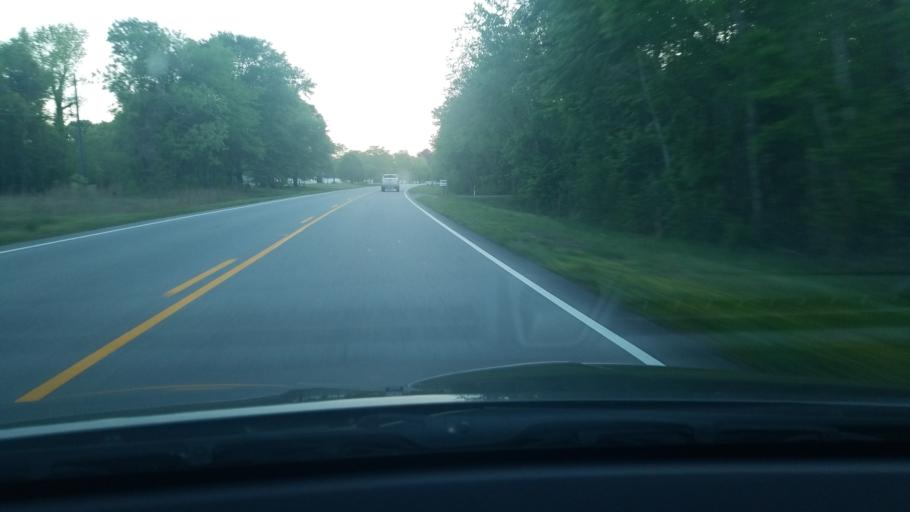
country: US
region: North Carolina
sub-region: Craven County
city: Vanceboro
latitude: 35.2344
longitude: -77.1062
